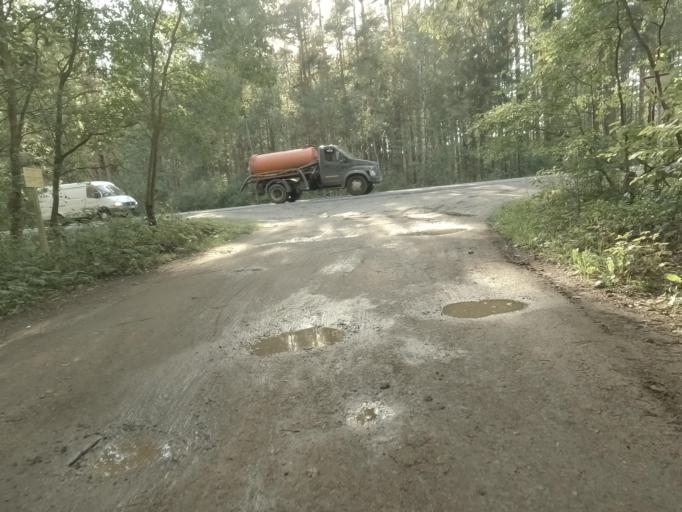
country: RU
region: Leningrad
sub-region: Volosovskiy Rayon
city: Shlissel'burg
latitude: 59.9453
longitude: 30.9853
